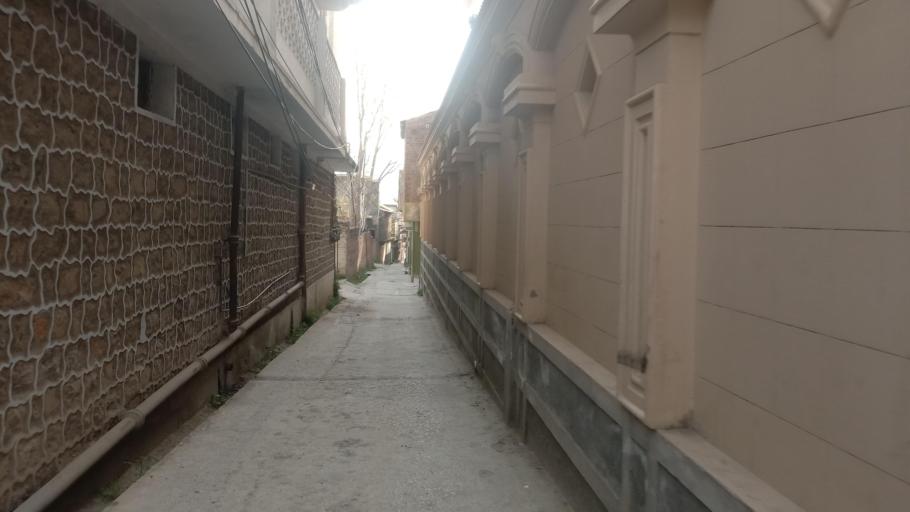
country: PK
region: Khyber Pakhtunkhwa
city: Abbottabad
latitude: 34.1635
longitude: 73.2639
